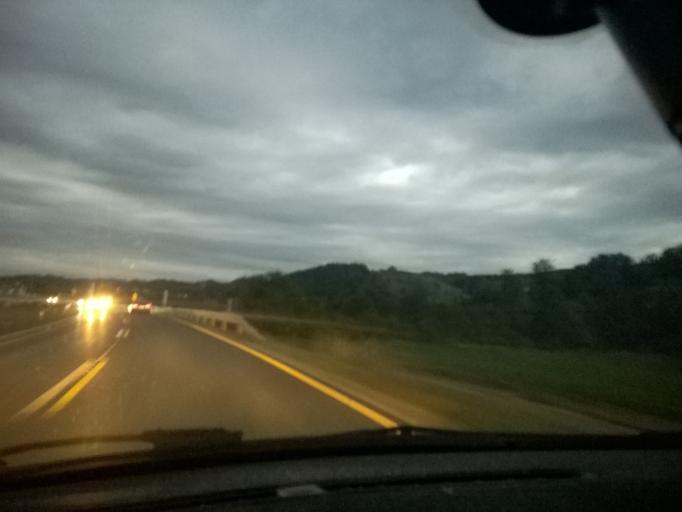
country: SI
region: Podlehnik
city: Podlehnik
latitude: 46.3085
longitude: 15.8650
